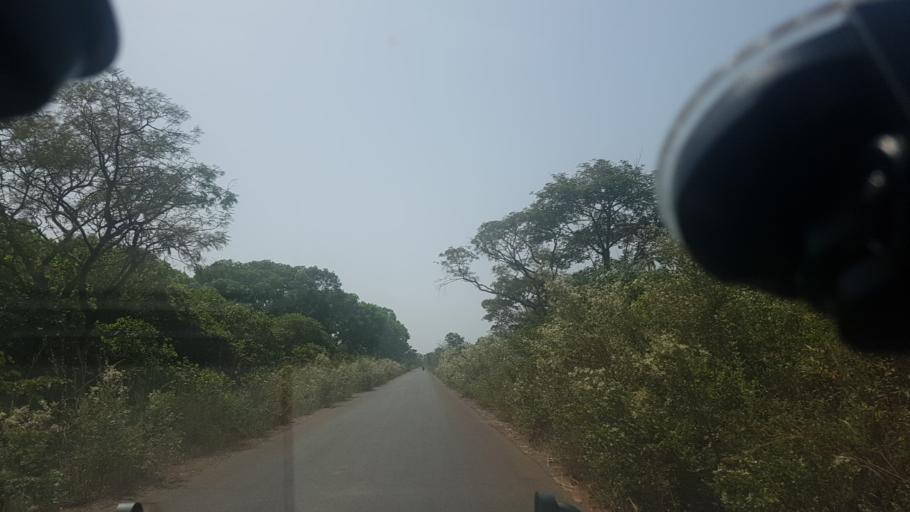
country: GW
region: Cacheu
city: Cacheu
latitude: 12.4099
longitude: -16.0329
